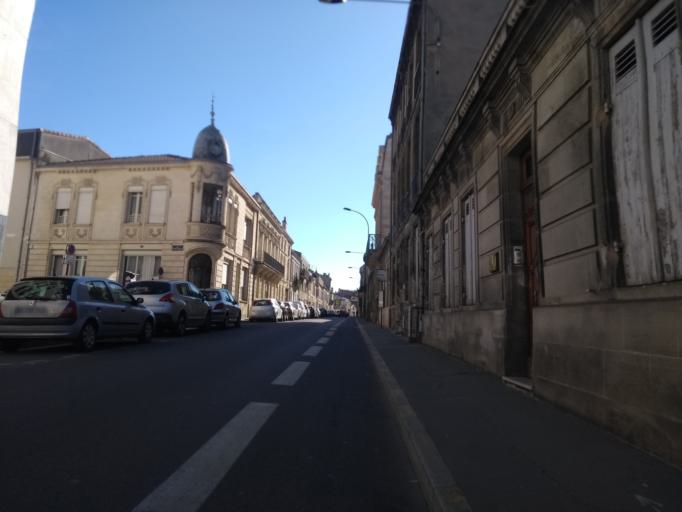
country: FR
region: Aquitaine
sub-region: Departement de la Gironde
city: Bordeaux
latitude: 44.8279
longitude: -0.5612
